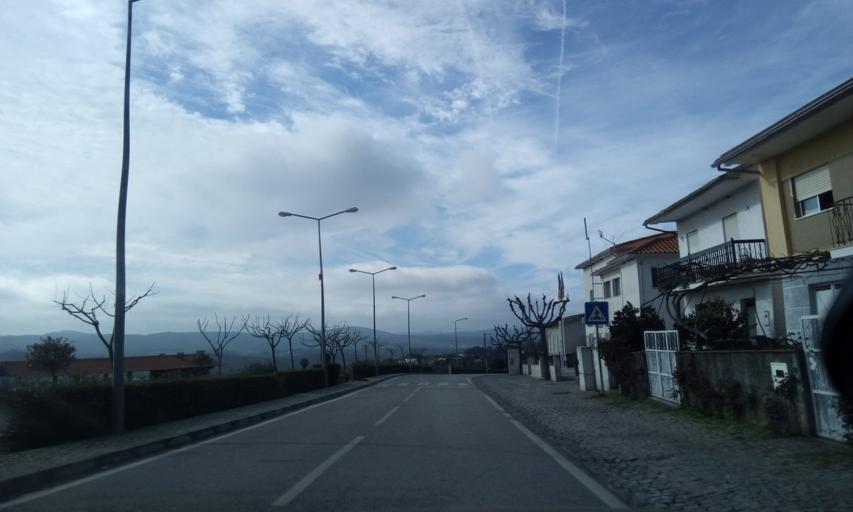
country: PT
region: Guarda
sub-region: Aguiar da Beira
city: Aguiar da Beira
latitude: 40.7377
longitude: -7.5552
